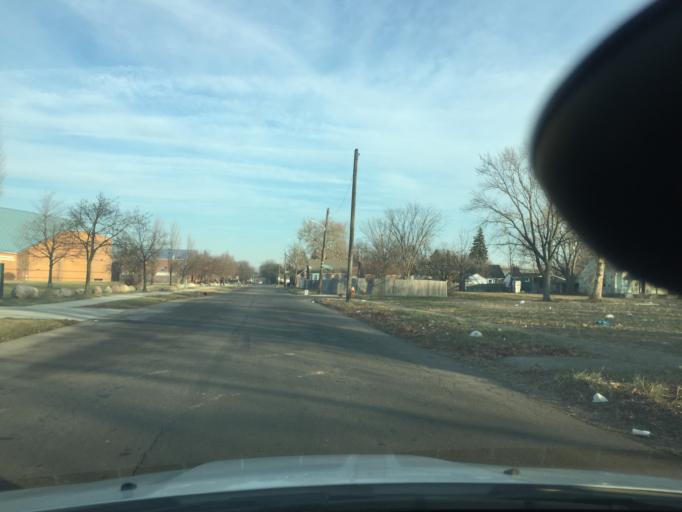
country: US
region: Michigan
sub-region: Macomb County
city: Eastpointe
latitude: 42.4395
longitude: -82.9608
